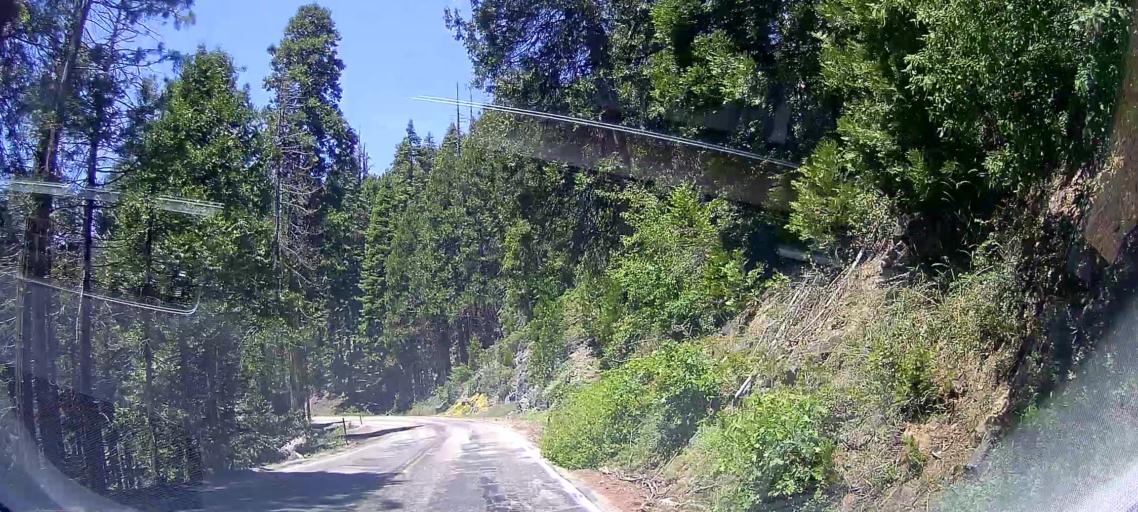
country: US
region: California
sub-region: Tulare County
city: Three Rivers
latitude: 36.7180
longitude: -118.9282
